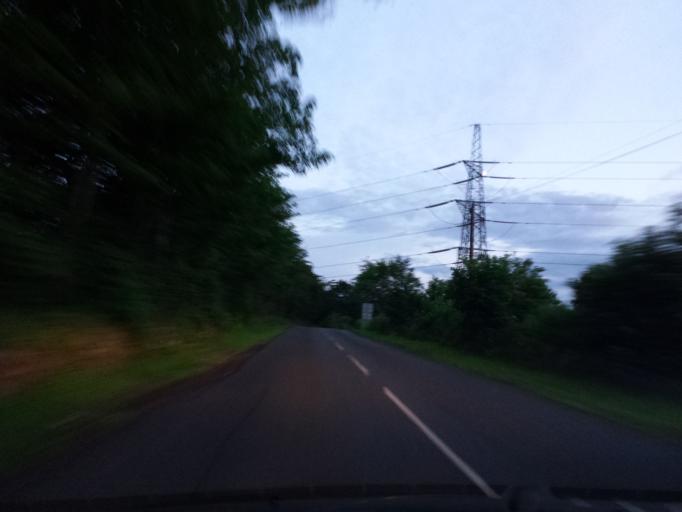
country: GB
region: Scotland
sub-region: The Scottish Borders
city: Duns
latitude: 55.7977
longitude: -2.3367
